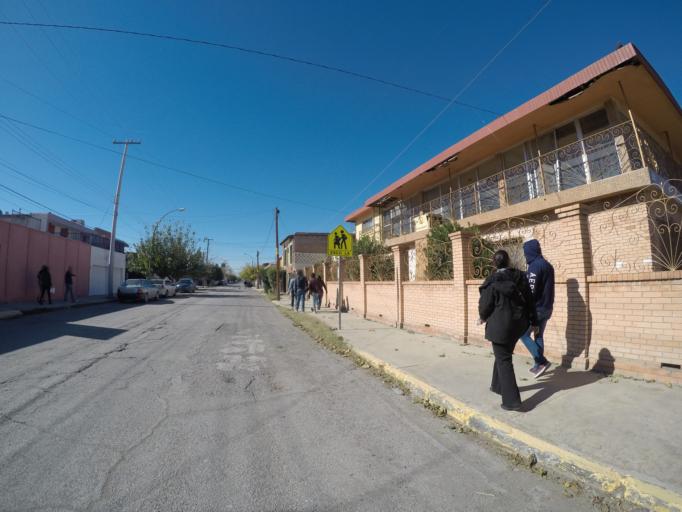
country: MX
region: Chihuahua
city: Ciudad Juarez
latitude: 31.7432
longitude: -106.4593
